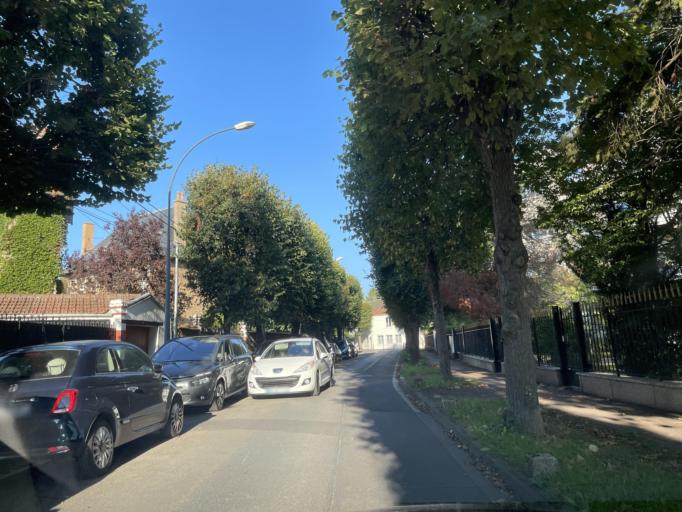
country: FR
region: Ile-de-France
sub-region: Departement du Val-de-Marne
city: Saint-Maur-des-Fosses
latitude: 48.7880
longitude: 2.5102
